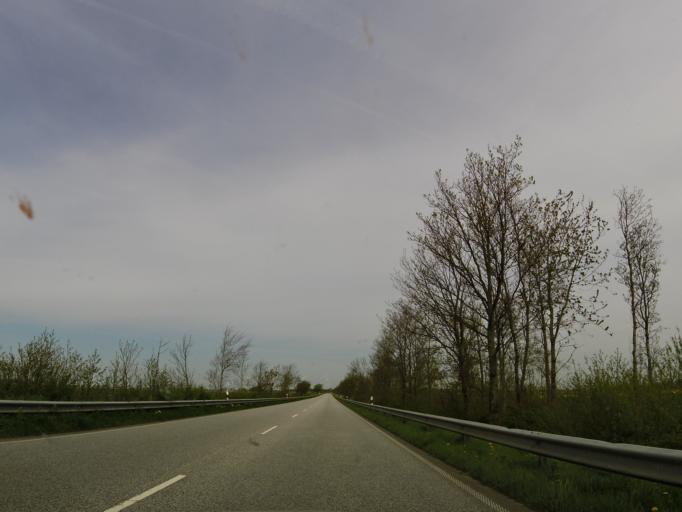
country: DE
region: Schleswig-Holstein
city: Norderwohrden
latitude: 54.2270
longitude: 9.0405
